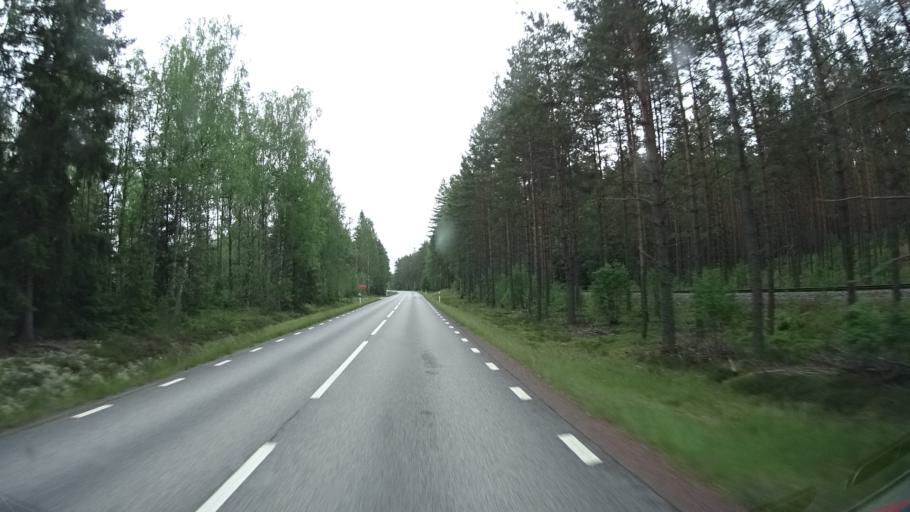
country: SE
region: Joenkoeping
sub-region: Eksjo Kommun
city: Mariannelund
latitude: 57.5647
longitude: 15.7057
